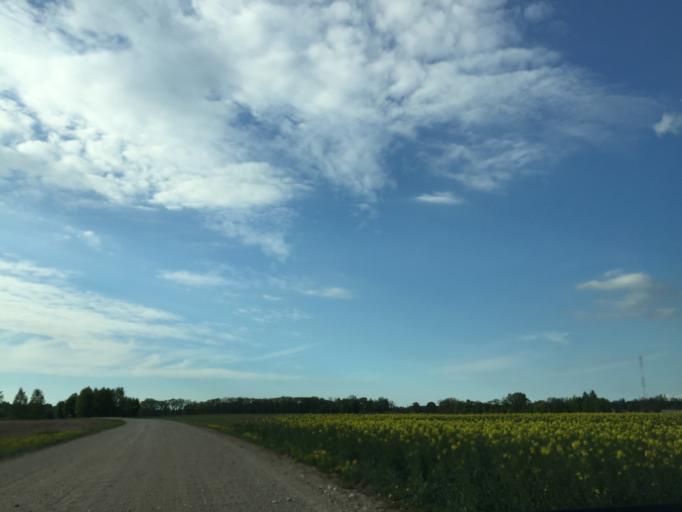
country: LV
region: Limbazu Rajons
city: Limbazi
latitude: 57.3711
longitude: 24.6902
